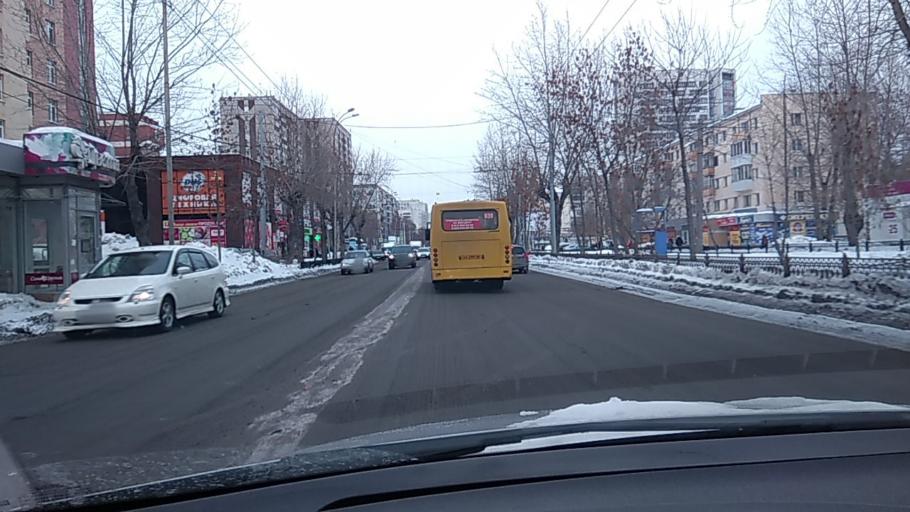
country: RU
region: Sverdlovsk
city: Yekaterinburg
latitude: 56.8084
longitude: 60.6238
